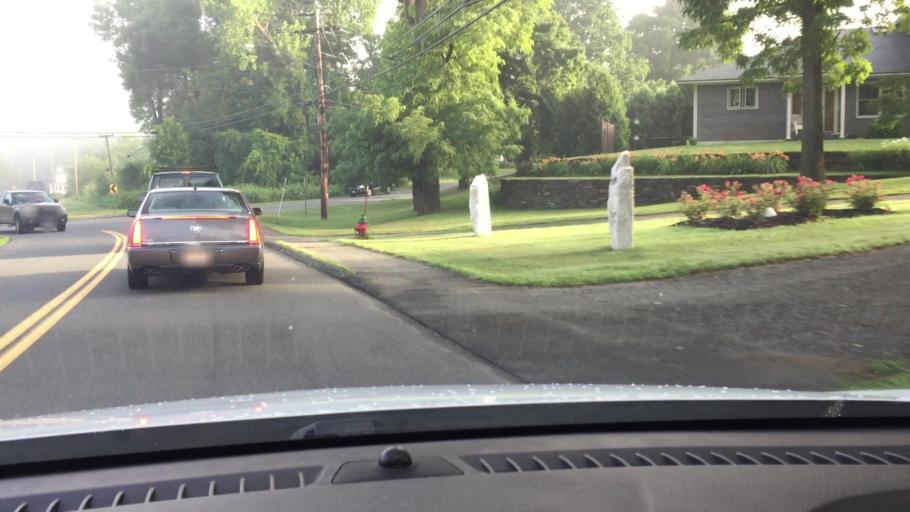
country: US
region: Massachusetts
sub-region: Berkshire County
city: Lee
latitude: 42.3253
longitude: -73.2393
